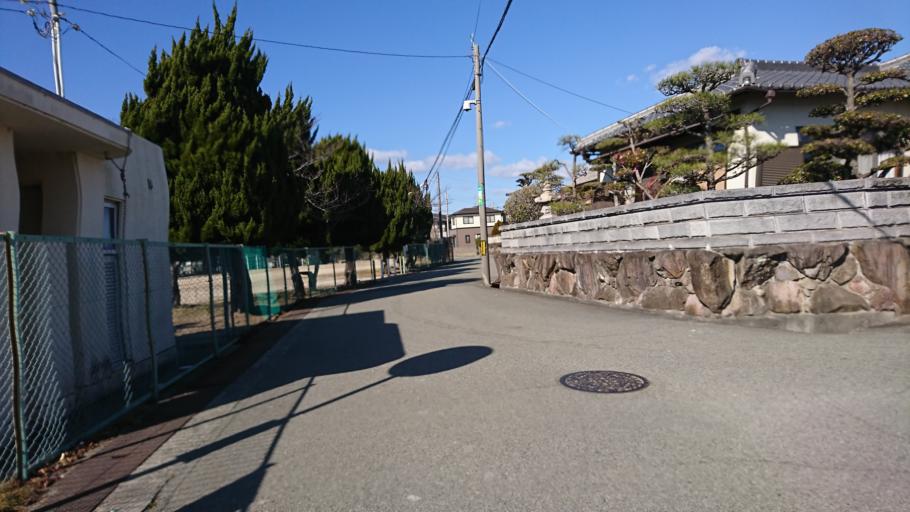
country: JP
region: Hyogo
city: Kakogawacho-honmachi
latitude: 34.7308
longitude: 134.8565
